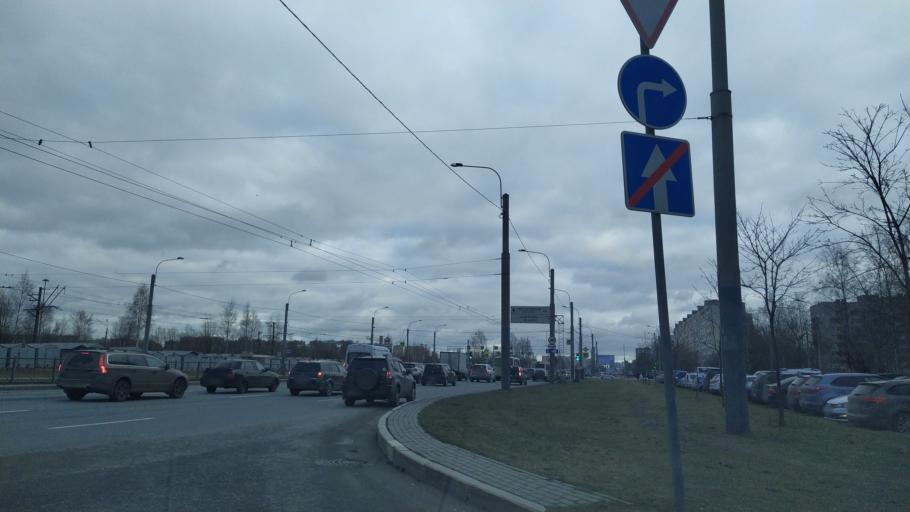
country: RU
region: Leningrad
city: Bugry
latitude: 60.0506
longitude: 30.3904
